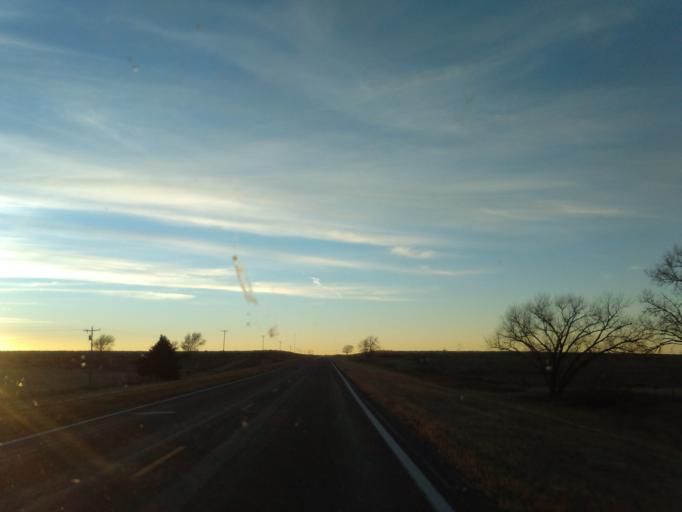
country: US
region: Kansas
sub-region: Wallace County
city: Sharon Springs
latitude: 38.9021
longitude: -101.7023
